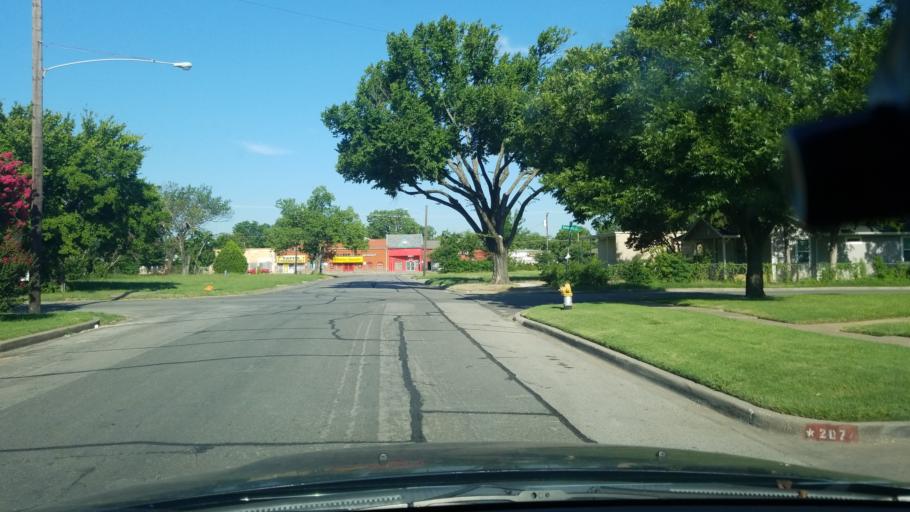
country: US
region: Texas
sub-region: Dallas County
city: Dallas
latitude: 32.7229
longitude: -96.8213
